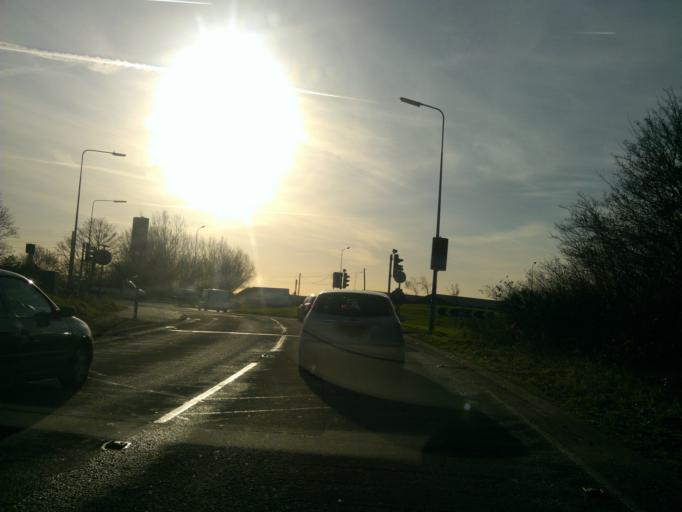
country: GB
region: England
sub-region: Essex
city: Chelmsford
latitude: 51.7567
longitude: 0.5229
